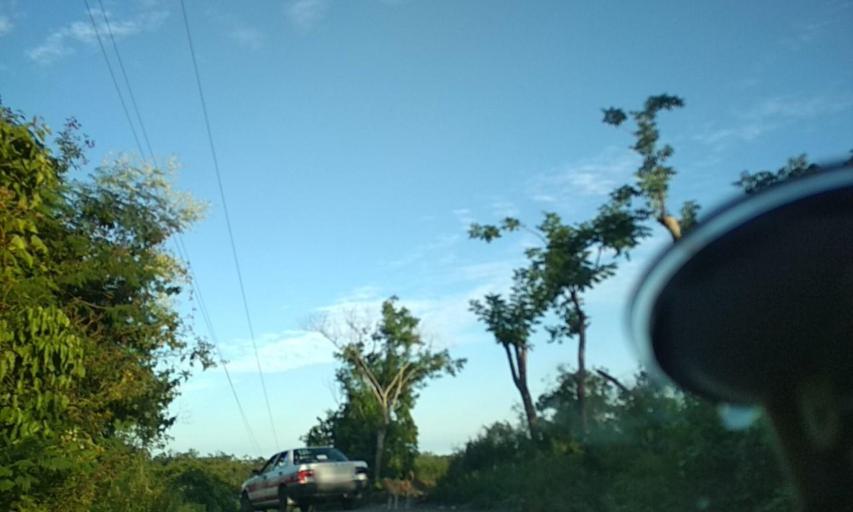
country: MX
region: Veracruz
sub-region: Poza Rica de Hidalgo
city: El Mollejon
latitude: 20.5423
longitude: -97.3971
